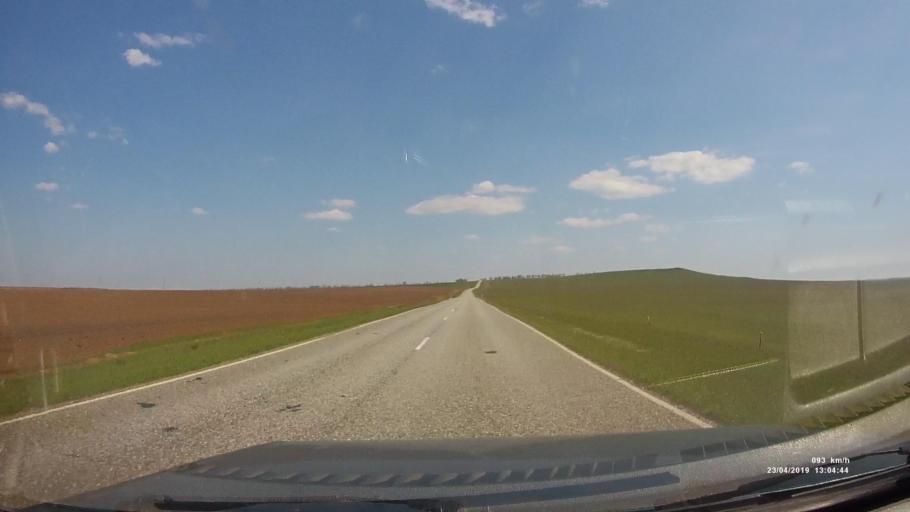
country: RU
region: Kalmykiya
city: Yashalta
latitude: 46.5932
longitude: 42.7094
